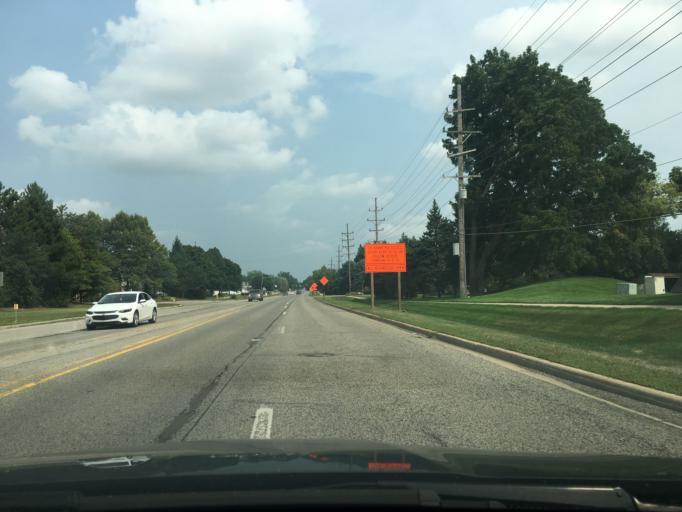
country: US
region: Michigan
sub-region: Oakland County
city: Bloomfield Hills
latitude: 42.6203
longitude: -83.2310
